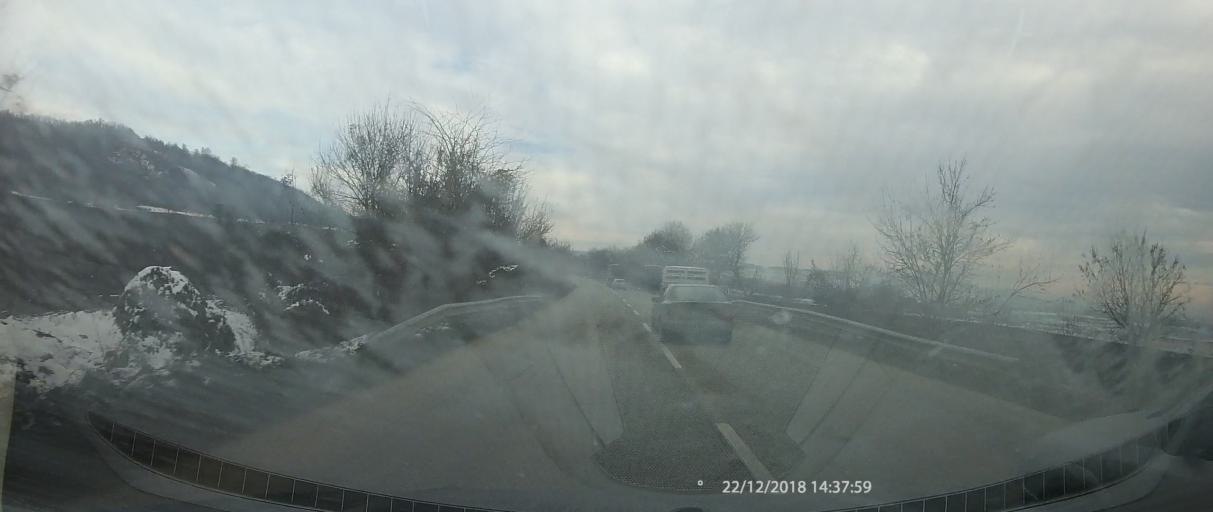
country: BG
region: Pleven
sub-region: Obshtina Levski
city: Levski
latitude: 43.4176
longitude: 25.1394
